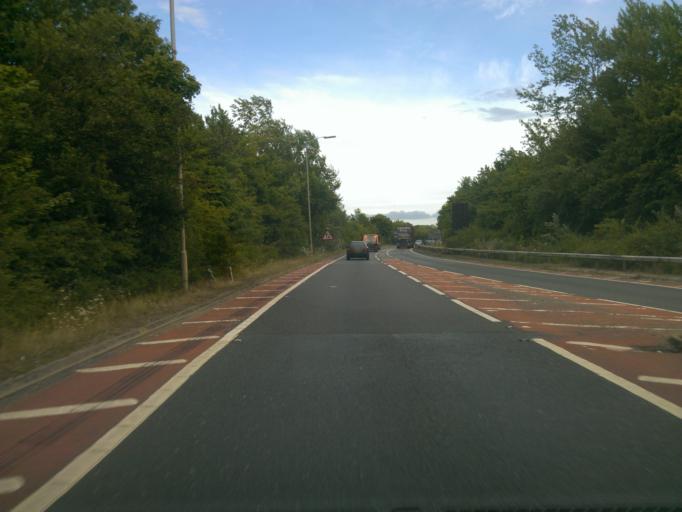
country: GB
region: England
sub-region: Essex
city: Coggeshall
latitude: 51.8798
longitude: 0.6949
